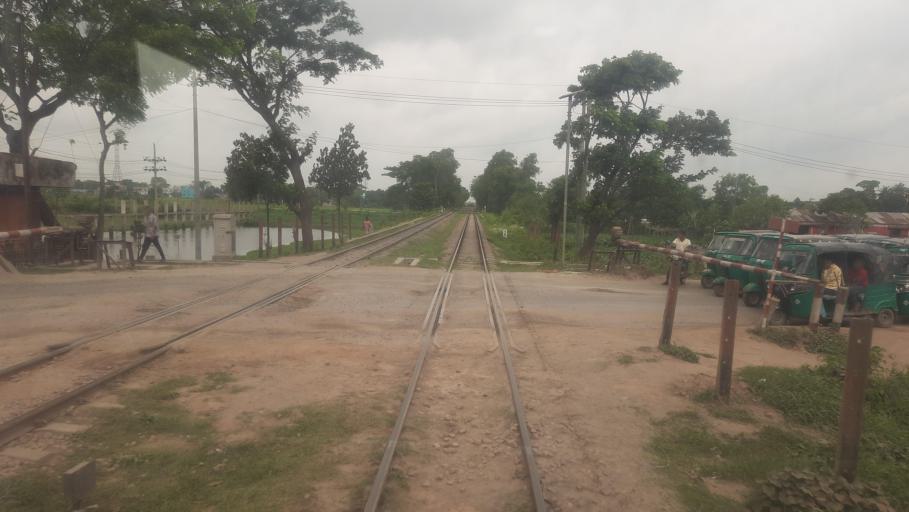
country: BD
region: Dhaka
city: Bhairab Bazar
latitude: 23.9660
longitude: 91.1016
